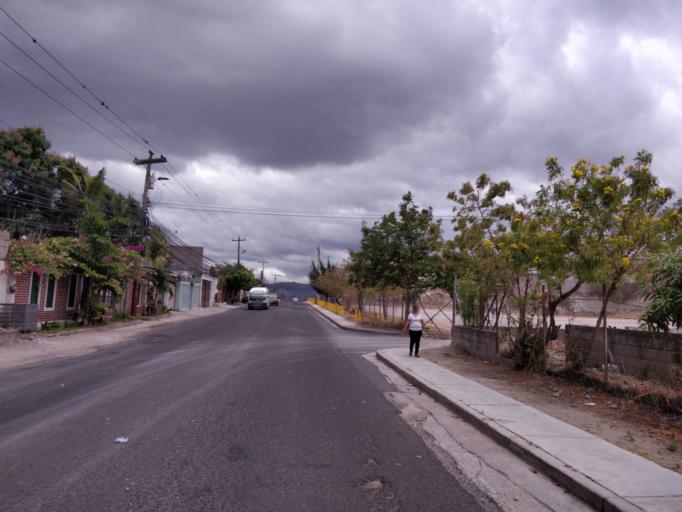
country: HN
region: Francisco Morazan
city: Yaguacire
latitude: 14.0477
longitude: -87.2202
